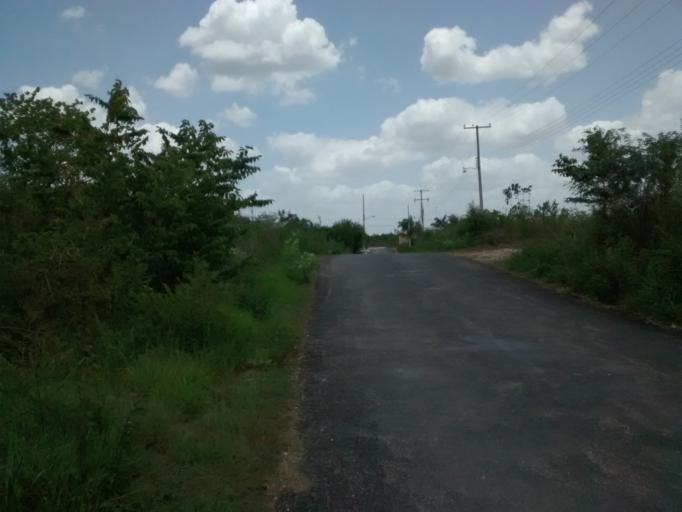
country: MX
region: Yucatan
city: Valladolid
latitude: 20.7002
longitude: -88.2197
